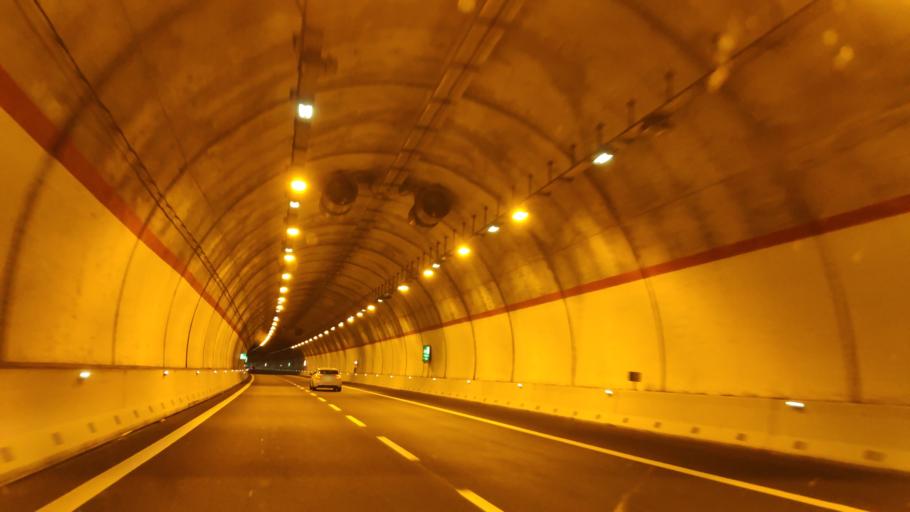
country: IT
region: Campania
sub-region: Provincia di Salerno
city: Buonabitacolo
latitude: 40.2545
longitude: 15.6605
